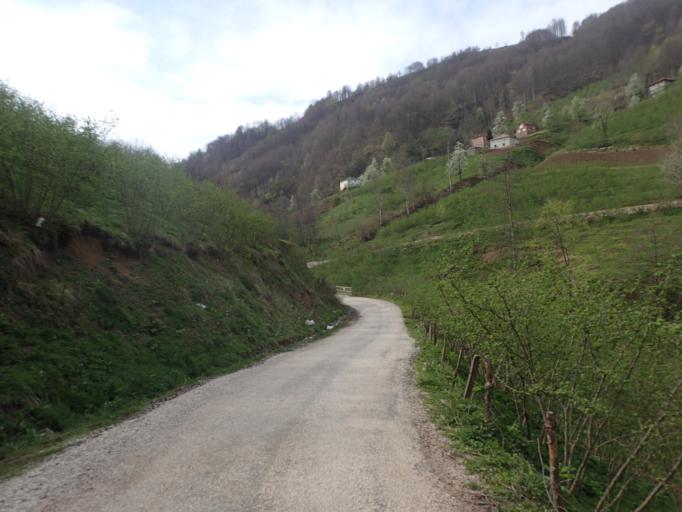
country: TR
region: Ordu
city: Aybasti
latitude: 40.6977
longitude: 37.2791
